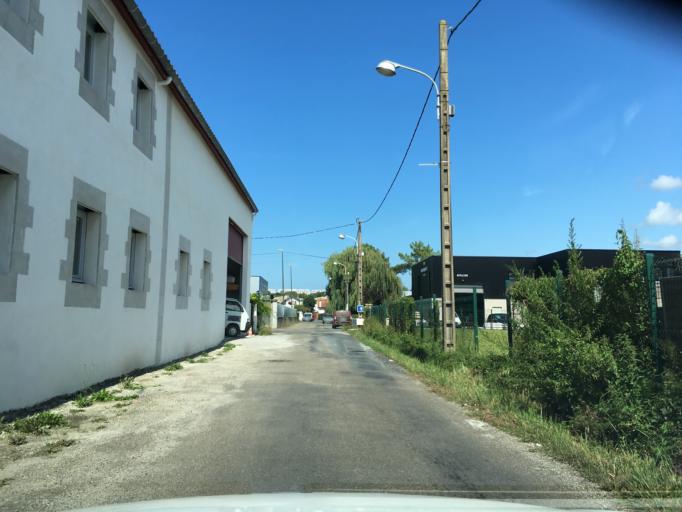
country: FR
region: Aquitaine
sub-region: Departement des Pyrenees-Atlantiques
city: Bayonne
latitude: 43.4878
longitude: -1.4529
